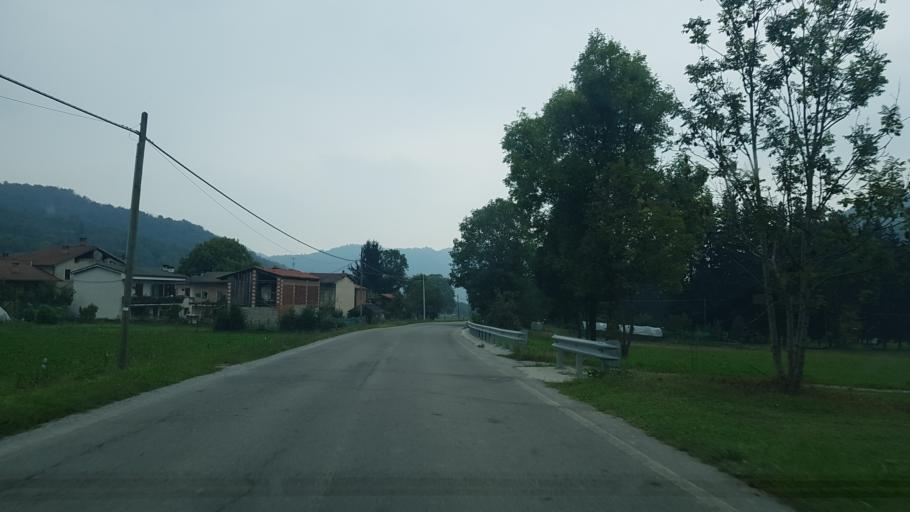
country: IT
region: Piedmont
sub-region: Provincia di Cuneo
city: Roccaforte Mondovi
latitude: 44.2987
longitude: 7.7460
